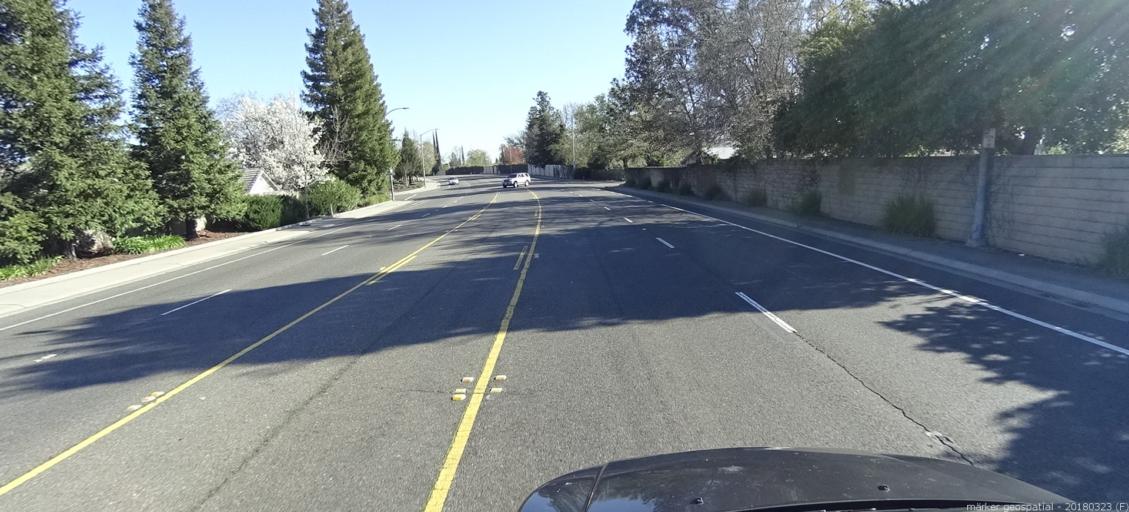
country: US
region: California
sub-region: Sacramento County
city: Antelope
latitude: 38.7007
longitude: -121.3470
